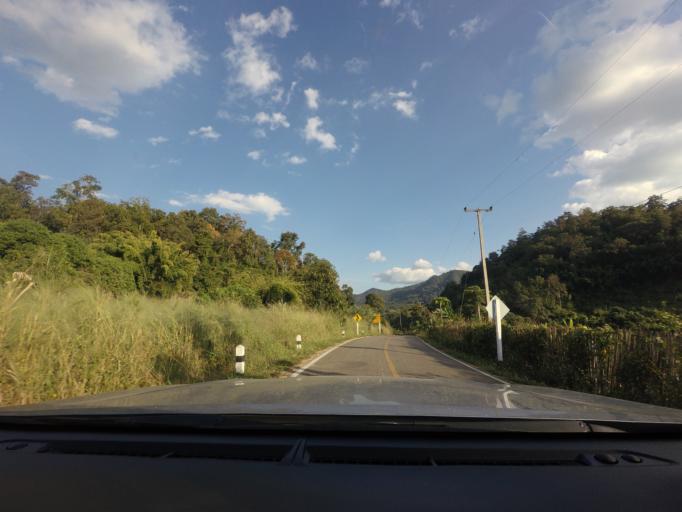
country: TH
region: Chiang Mai
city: Phrao
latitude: 19.5144
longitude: 99.1673
